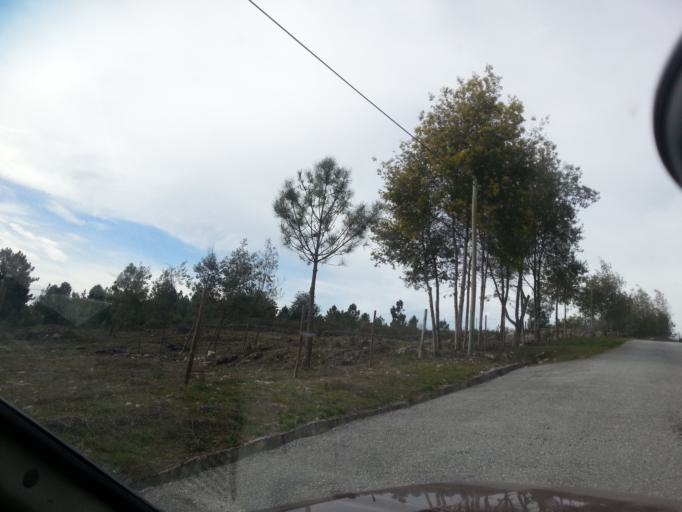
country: PT
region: Guarda
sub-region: Fornos de Algodres
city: Fornos de Algodres
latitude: 40.6073
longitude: -7.5431
